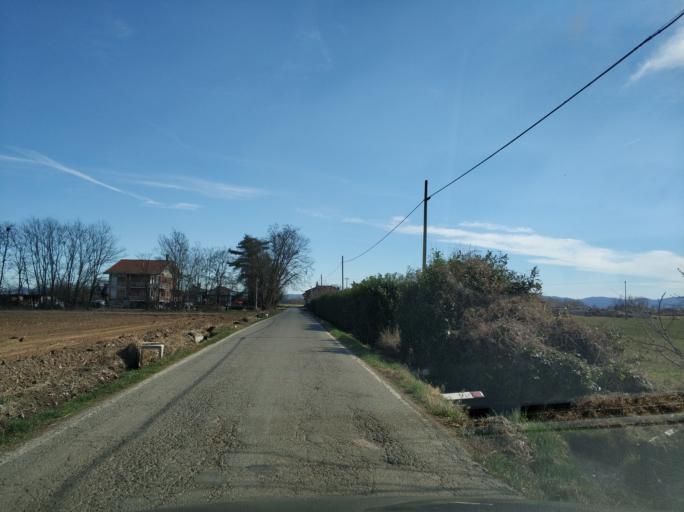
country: IT
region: Piedmont
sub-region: Provincia di Torino
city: San Francesco al Campo
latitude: 45.2016
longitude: 7.6719
